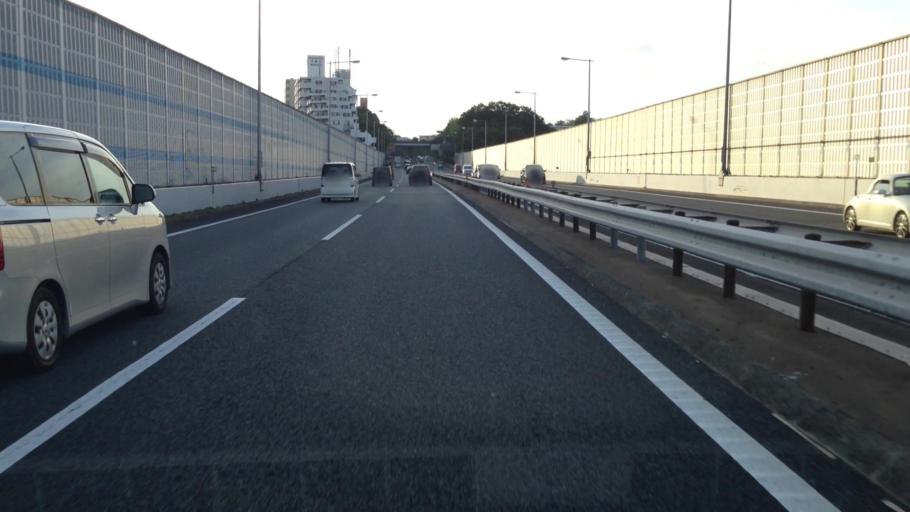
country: JP
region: Kanagawa
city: Kamakura
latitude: 35.3851
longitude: 139.5811
